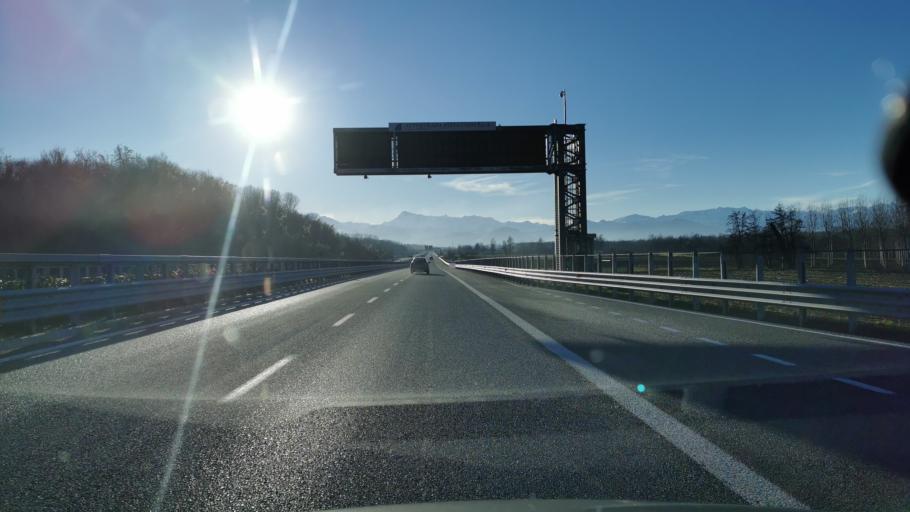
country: IT
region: Piedmont
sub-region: Provincia di Cuneo
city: Castelletto Stura
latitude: 44.4422
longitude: 7.6299
